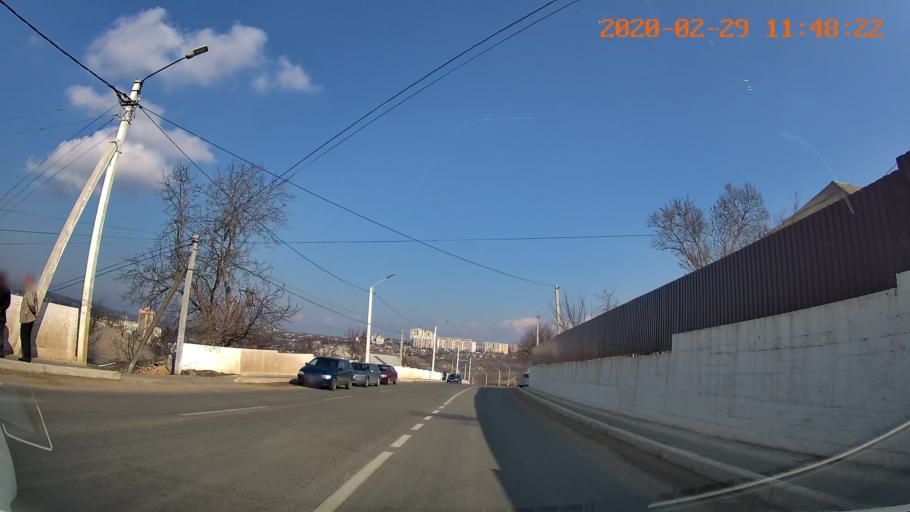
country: MD
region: Rezina
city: Rezina
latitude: 47.7477
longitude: 28.9900
